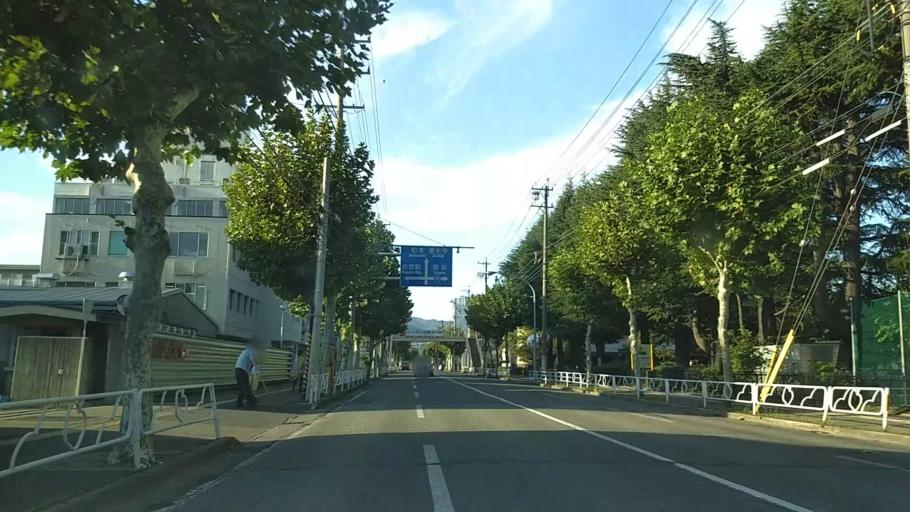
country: JP
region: Nagano
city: Nagano-shi
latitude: 36.6402
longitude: 138.1992
